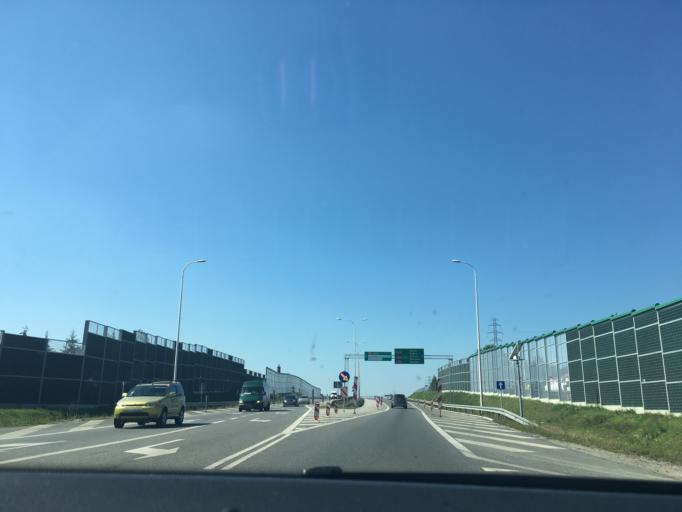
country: PL
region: Lublin Voivodeship
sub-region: Powiat lubelski
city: Jakubowice Murowane
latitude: 51.3095
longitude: 22.5968
